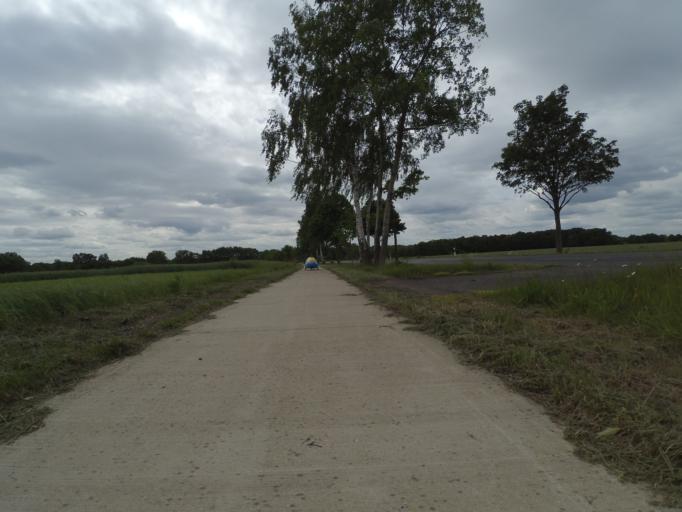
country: DE
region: Lower Saxony
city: Garbsen
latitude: 52.4375
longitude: 9.5224
